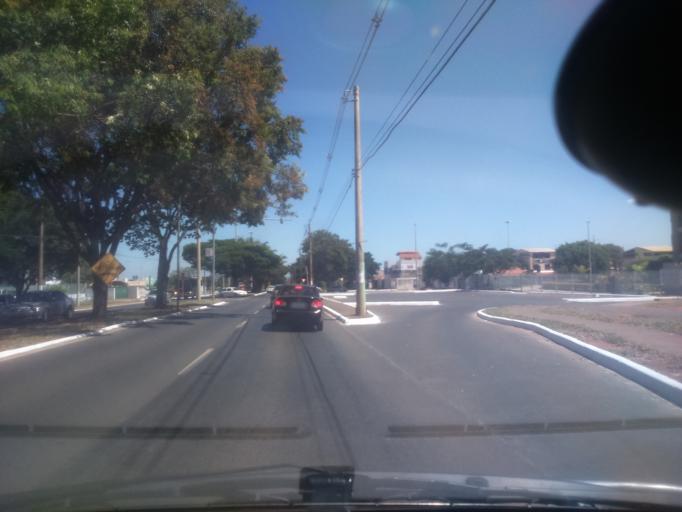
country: BR
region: Federal District
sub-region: Brasilia
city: Brasilia
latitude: -16.0093
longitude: -48.0609
